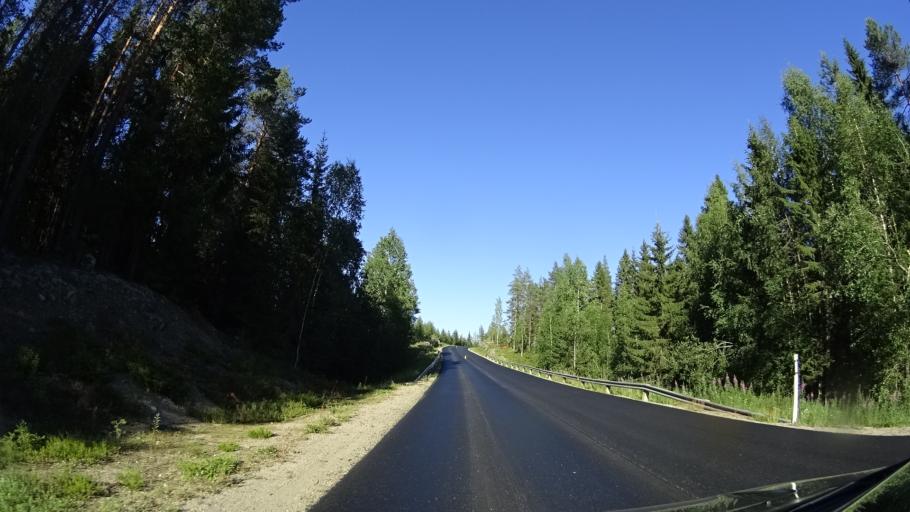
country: FI
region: North Karelia
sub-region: Pielisen Karjala
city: Valtimo
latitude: 63.5600
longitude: 28.6053
